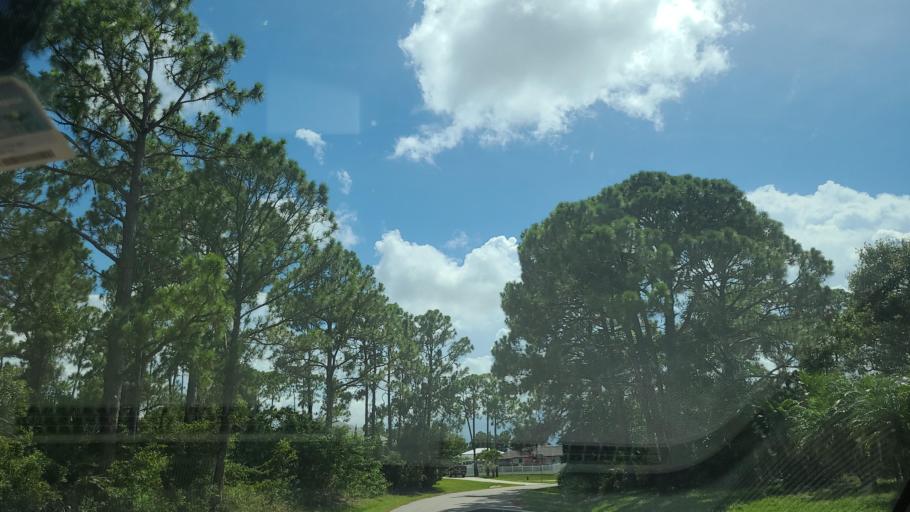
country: US
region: Florida
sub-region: Indian River County
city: Sebastian
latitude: 27.7771
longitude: -80.4927
